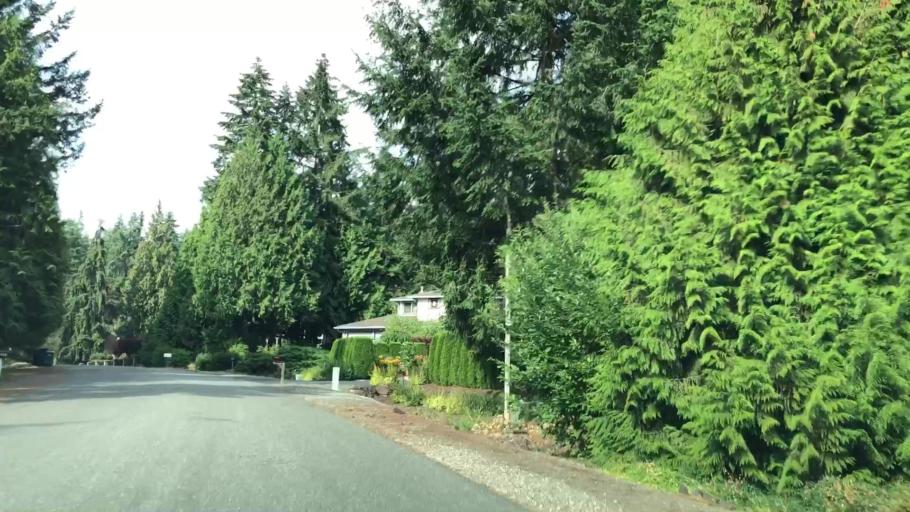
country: US
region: Washington
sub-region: King County
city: Cottage Lake
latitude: 47.7351
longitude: -122.0963
